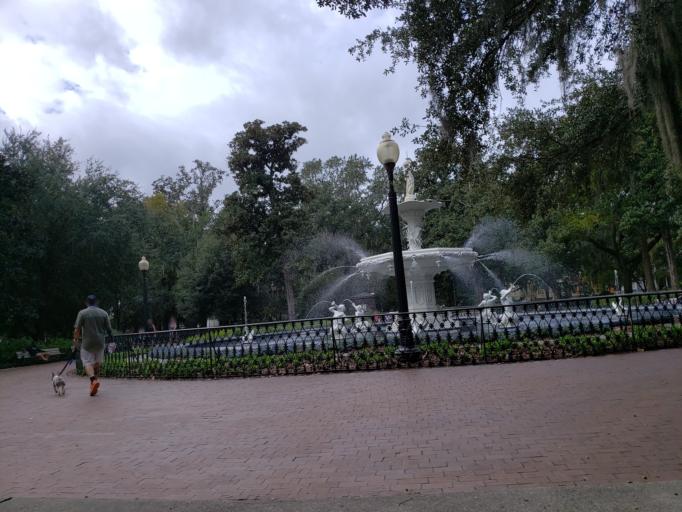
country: US
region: Georgia
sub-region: Chatham County
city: Savannah
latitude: 32.0693
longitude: -81.0954
